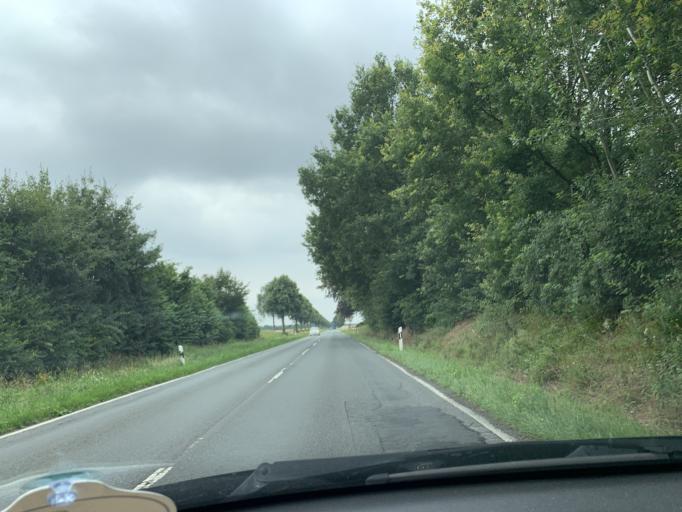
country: DE
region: North Rhine-Westphalia
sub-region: Regierungsbezirk Munster
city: Warendorf
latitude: 51.9924
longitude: 7.9501
